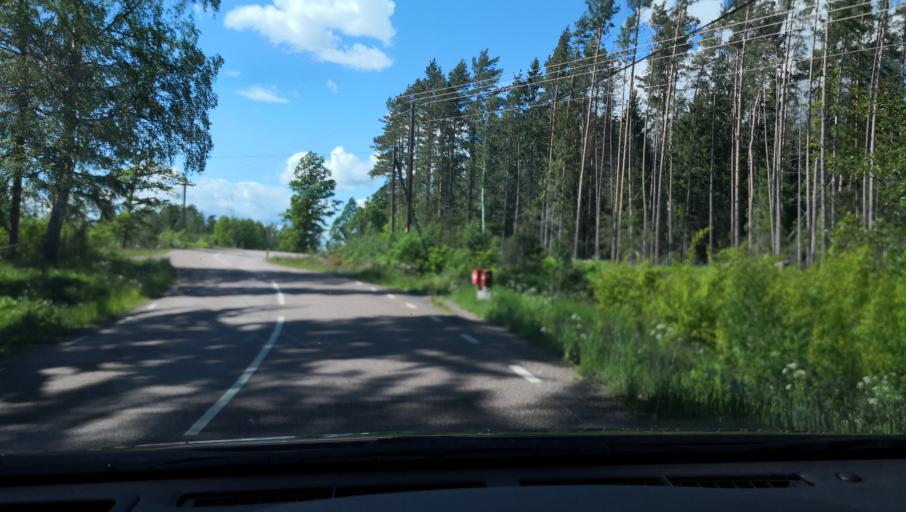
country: SE
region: Vaestmanland
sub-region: Arboga Kommun
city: Tyringe
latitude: 59.2998
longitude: 16.0217
